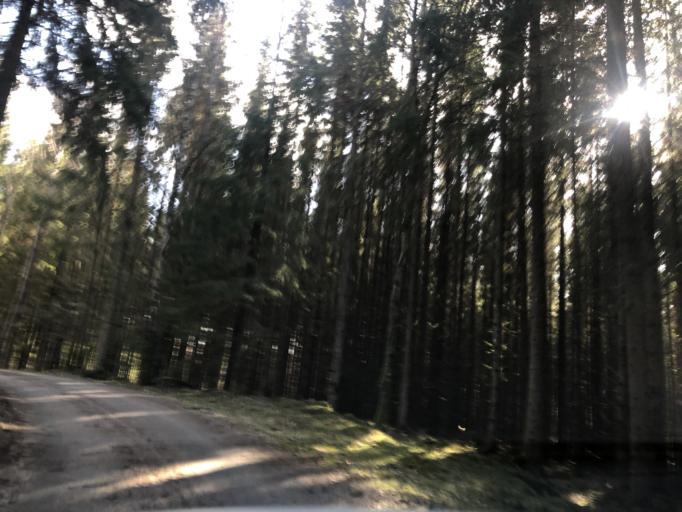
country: SE
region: Vaestra Goetaland
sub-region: Ulricehamns Kommun
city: Ulricehamn
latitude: 57.6902
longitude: 13.3762
